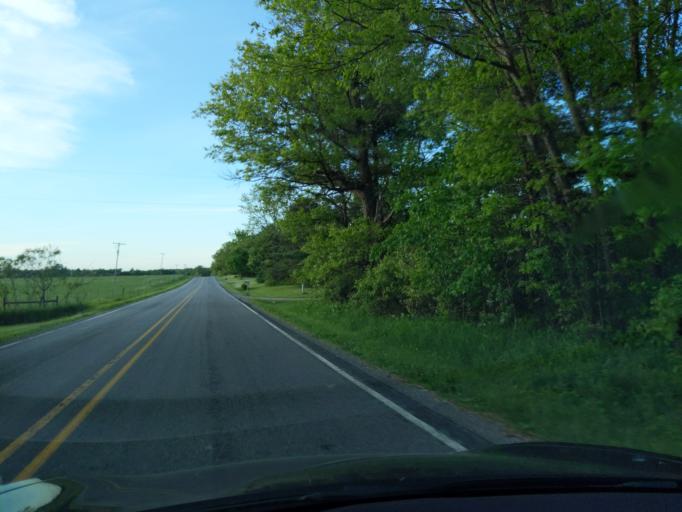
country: US
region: Michigan
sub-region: Ingham County
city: Leslie
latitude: 42.4857
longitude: -84.3169
